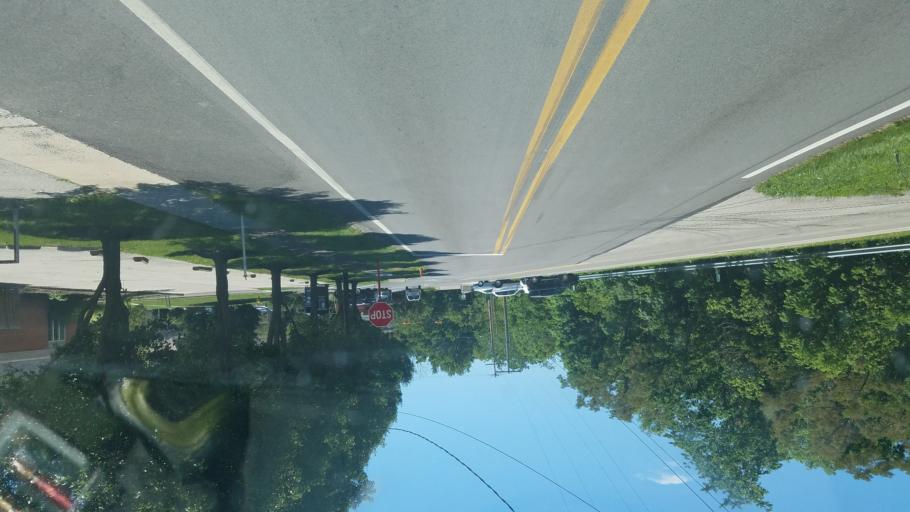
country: US
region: Ohio
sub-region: Delaware County
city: Sunbury
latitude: 40.2162
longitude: -82.8798
